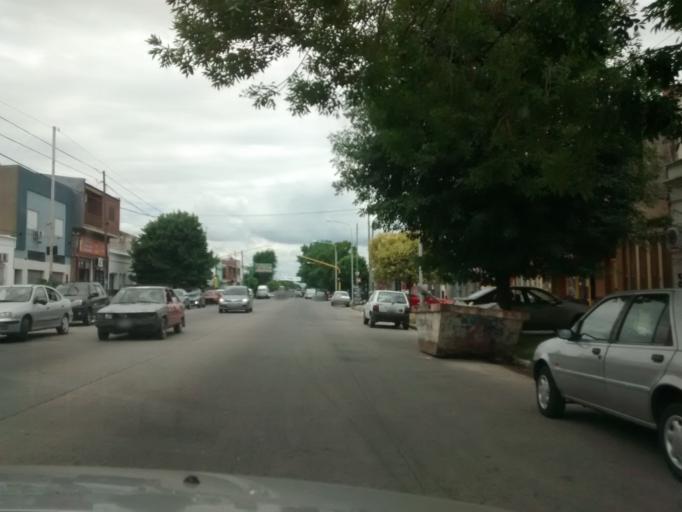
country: AR
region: Buenos Aires
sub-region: Partido de La Plata
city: La Plata
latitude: -34.9136
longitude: -57.9184
